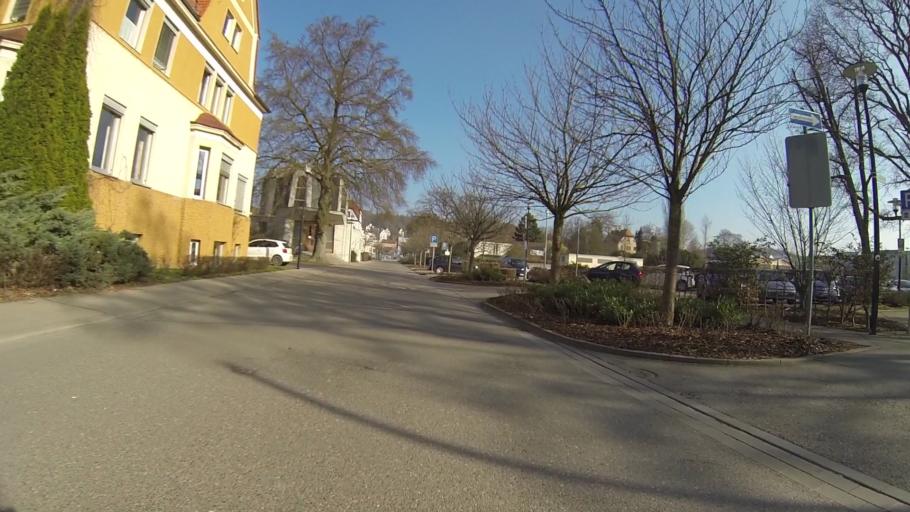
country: DE
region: Baden-Wuerttemberg
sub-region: Regierungsbezirk Stuttgart
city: Heidenheim an der Brenz
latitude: 48.6734
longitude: 10.1518
